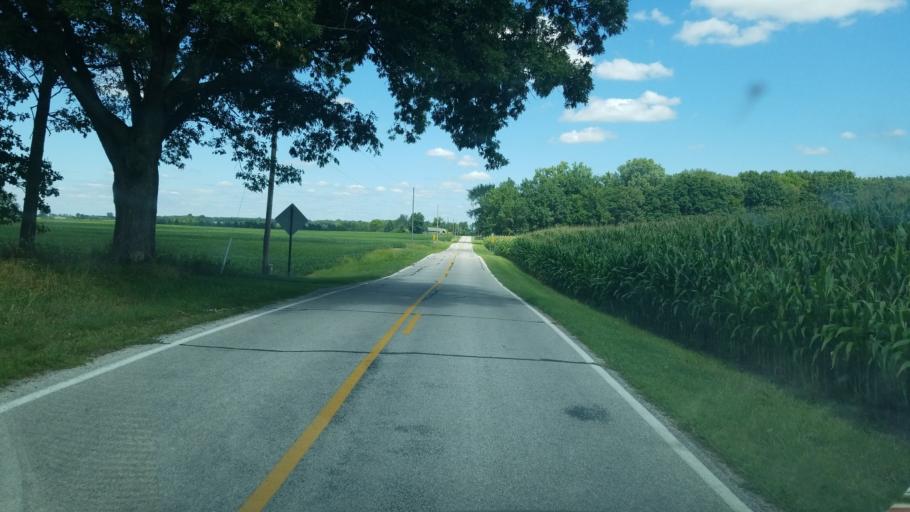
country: US
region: Ohio
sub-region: Fulton County
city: Delta
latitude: 41.6303
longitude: -84.0153
